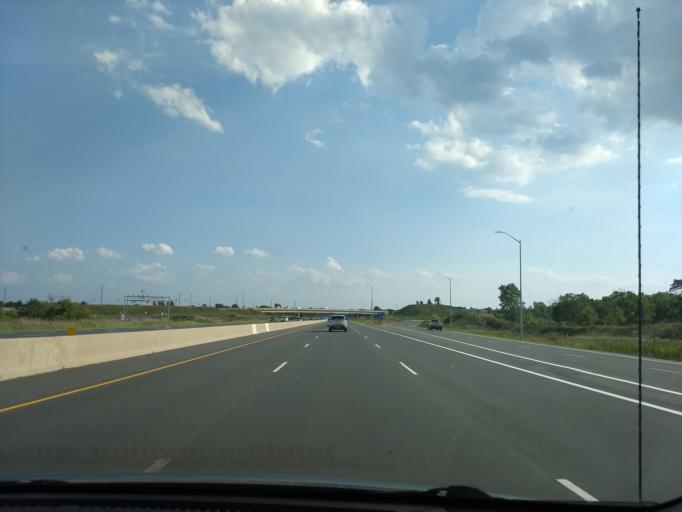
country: CA
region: Ontario
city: Burlington
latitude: 43.3877
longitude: -79.8339
